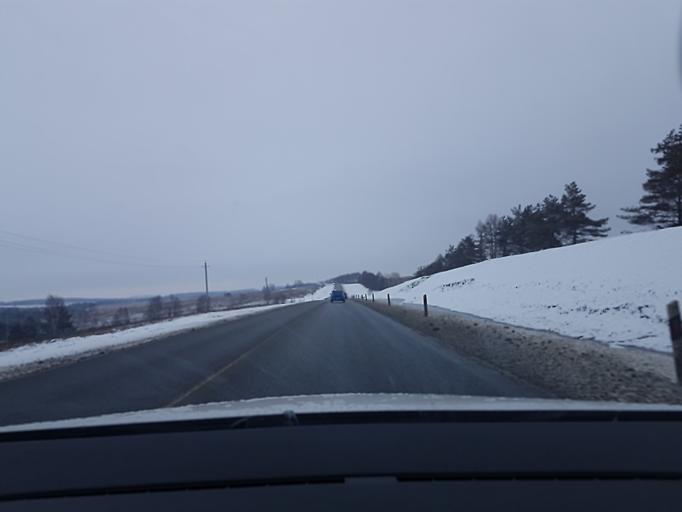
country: RU
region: Moskovskaya
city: Ozherel'ye
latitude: 54.7271
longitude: 38.2687
